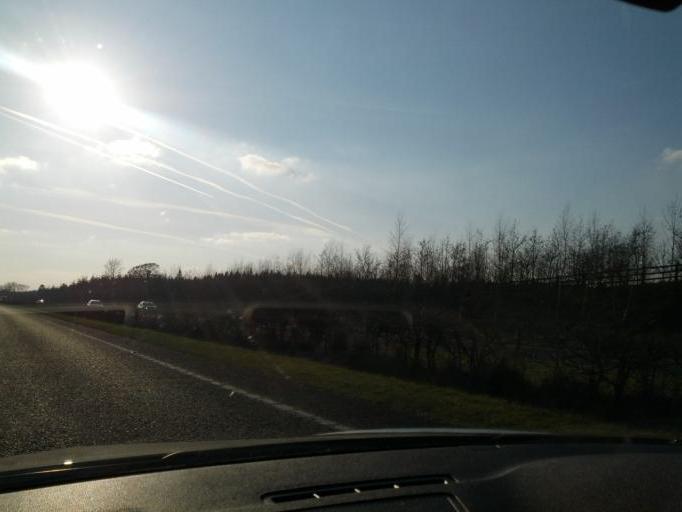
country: IE
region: Leinster
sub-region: Laois
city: Portarlington
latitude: 53.1043
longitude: -7.1405
